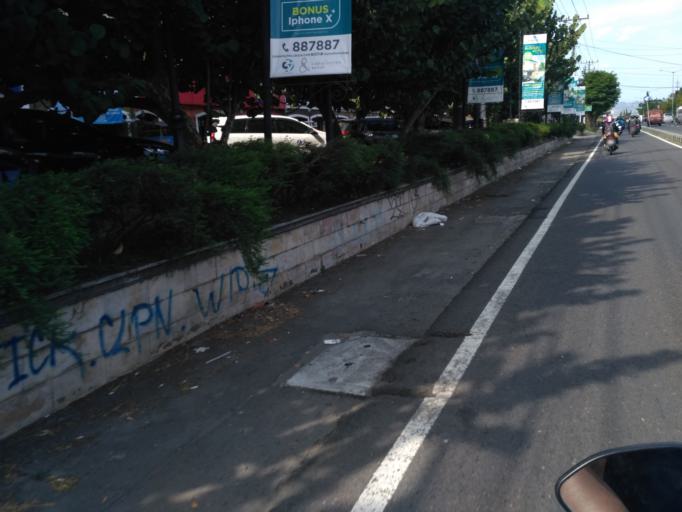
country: ID
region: Daerah Istimewa Yogyakarta
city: Depok
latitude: -7.7633
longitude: 110.4204
